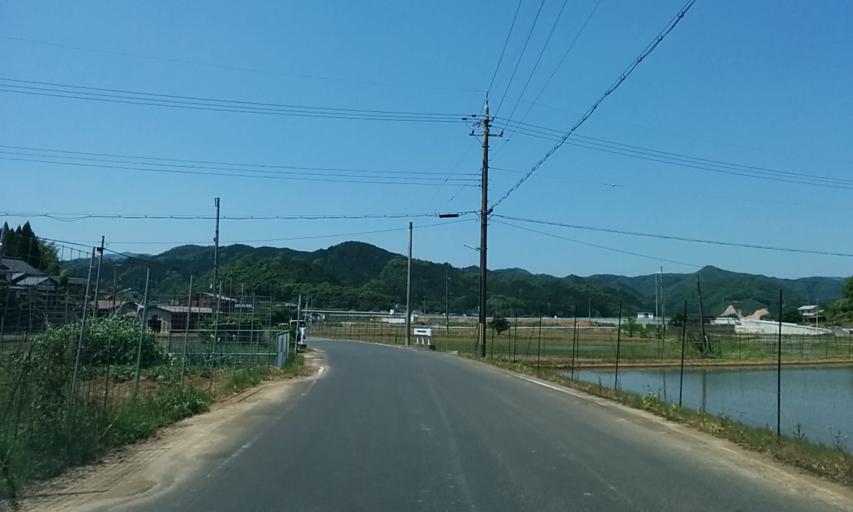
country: JP
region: Kyoto
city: Ayabe
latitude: 35.3859
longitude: 135.1836
